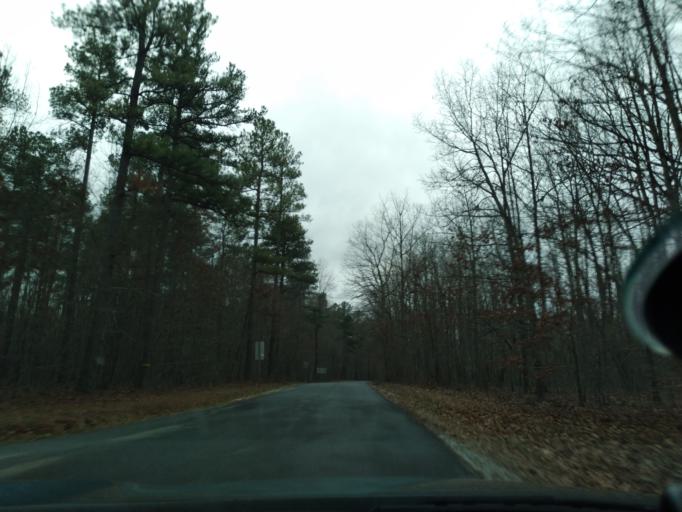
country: US
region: Virginia
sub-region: Appomattox County
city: Appomattox
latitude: 37.4154
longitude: -78.6737
